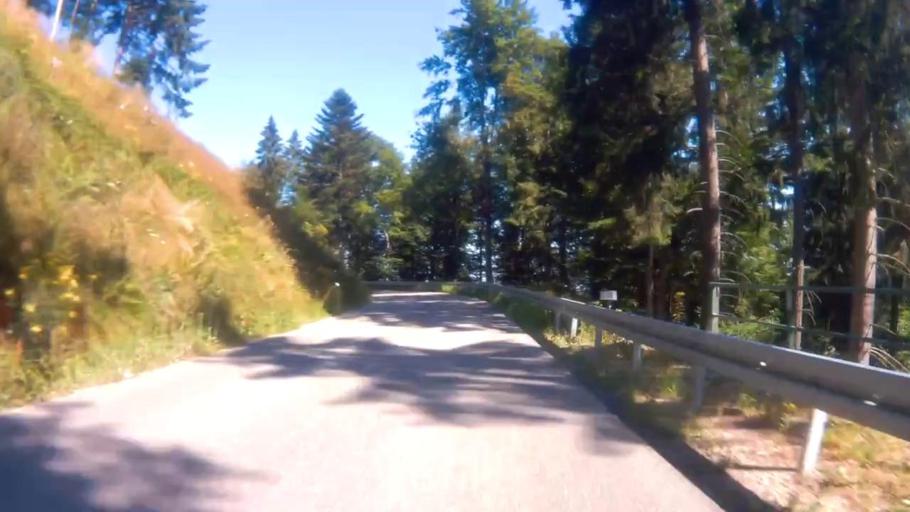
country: DE
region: Baden-Wuerttemberg
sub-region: Freiburg Region
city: Badenweiler
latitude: 47.7868
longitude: 7.7073
